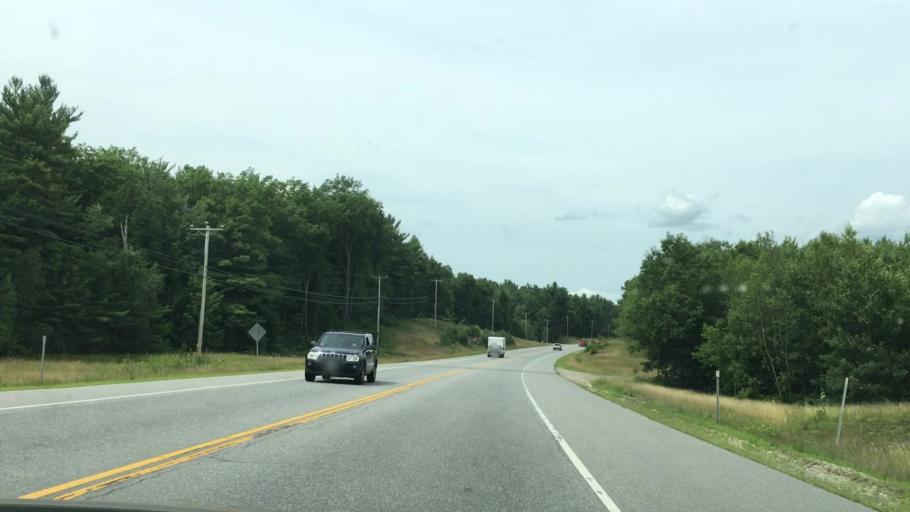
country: US
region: New Hampshire
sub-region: Cheshire County
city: Rindge
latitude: 42.7512
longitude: -72.0398
